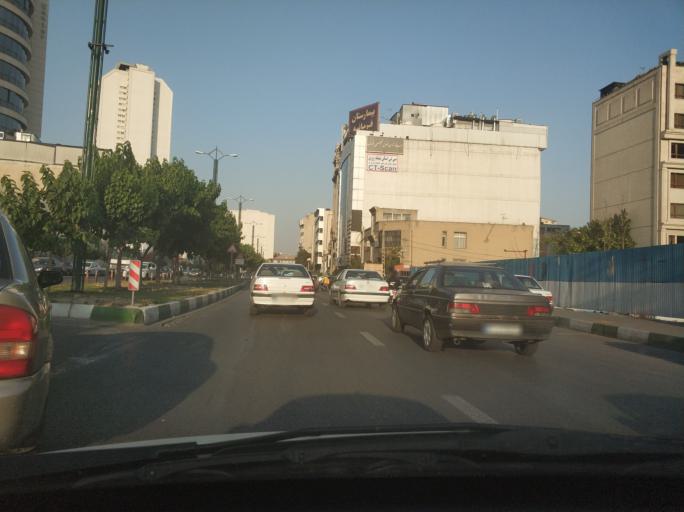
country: IR
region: Tehran
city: Tajrish
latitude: 35.7993
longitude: 51.4718
